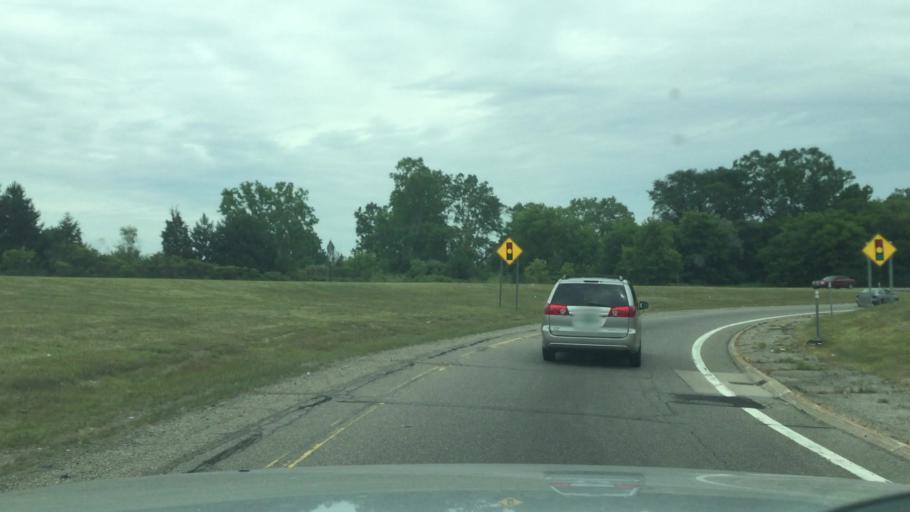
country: US
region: Michigan
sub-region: Genesee County
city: Flint
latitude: 43.0039
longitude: -83.7482
